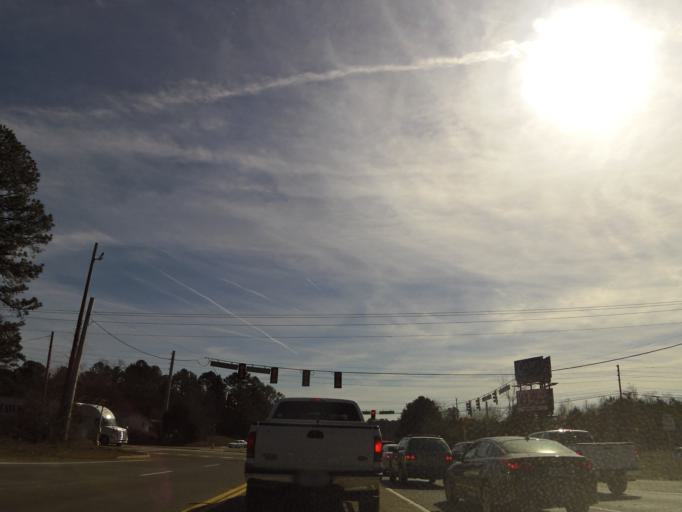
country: US
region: Georgia
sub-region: Whitfield County
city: Dalton
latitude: 34.7797
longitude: -84.9144
